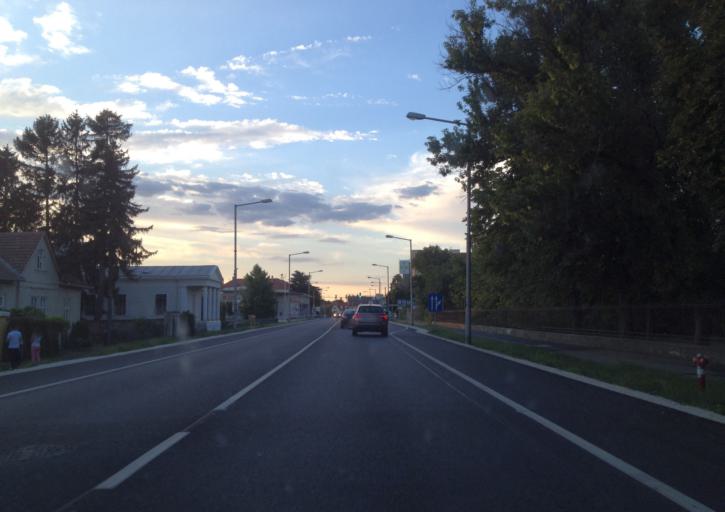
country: HU
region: Gyor-Moson-Sopron
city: Mosonmagyarovar
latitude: 47.8707
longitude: 17.2703
